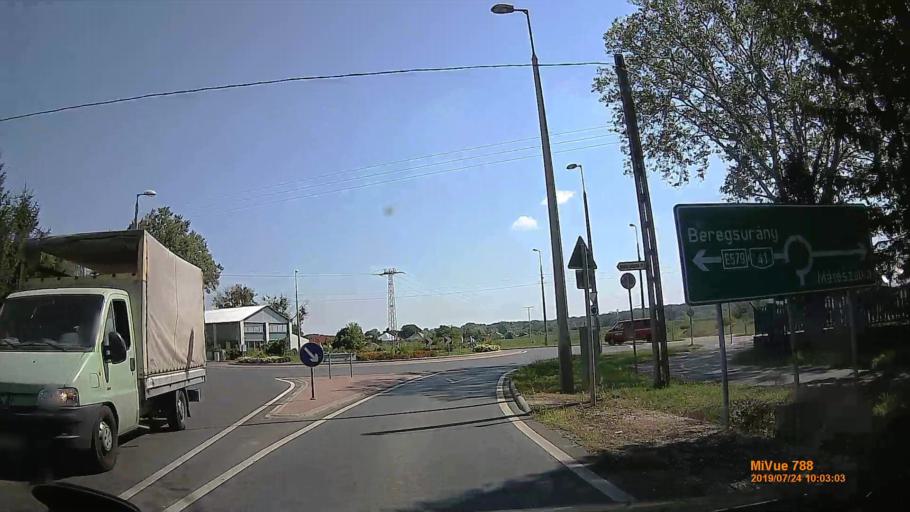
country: HU
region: Szabolcs-Szatmar-Bereg
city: Vasarosnameny
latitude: 48.1158
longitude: 22.3142
